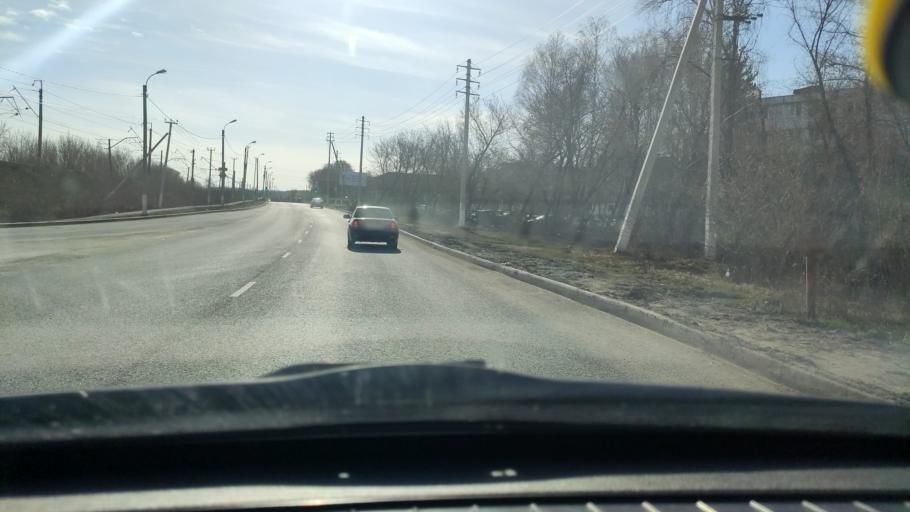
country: RU
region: Samara
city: Zhigulevsk
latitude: 53.4070
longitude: 49.4882
